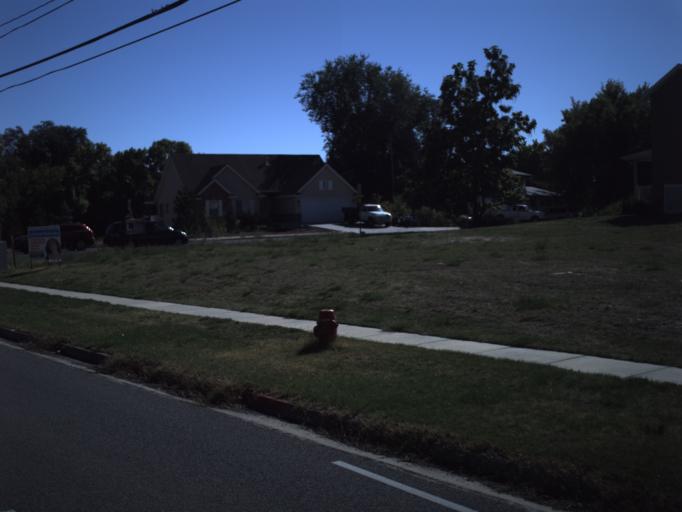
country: US
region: Utah
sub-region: Davis County
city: Fruit Heights
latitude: 41.0164
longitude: -111.9186
